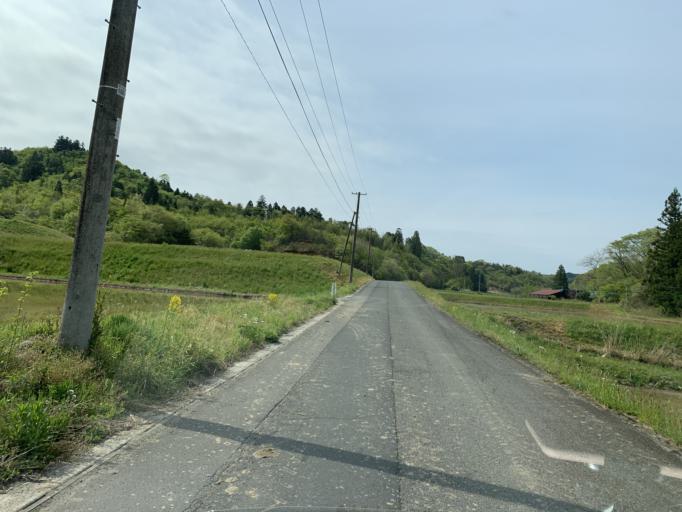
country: JP
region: Iwate
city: Ichinoseki
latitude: 38.8968
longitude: 141.0615
